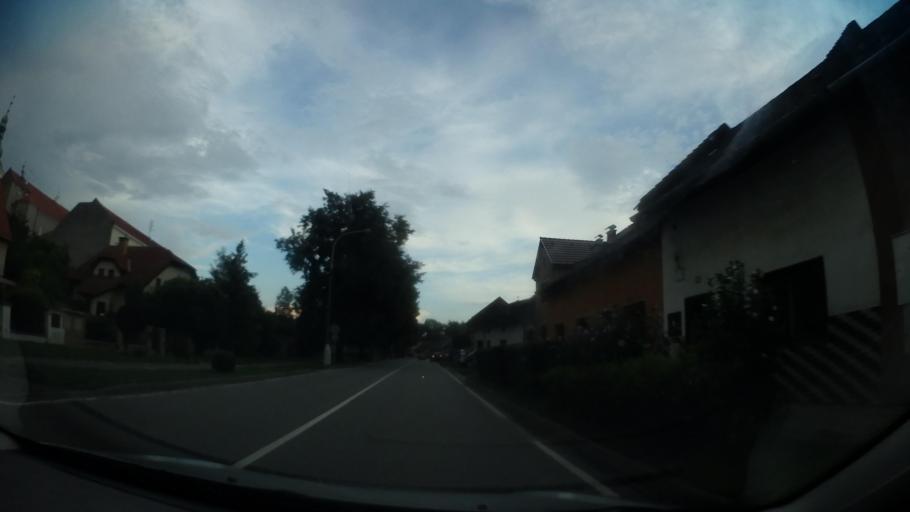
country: CZ
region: Olomoucky
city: Tovacov
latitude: 49.4275
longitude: 17.2882
